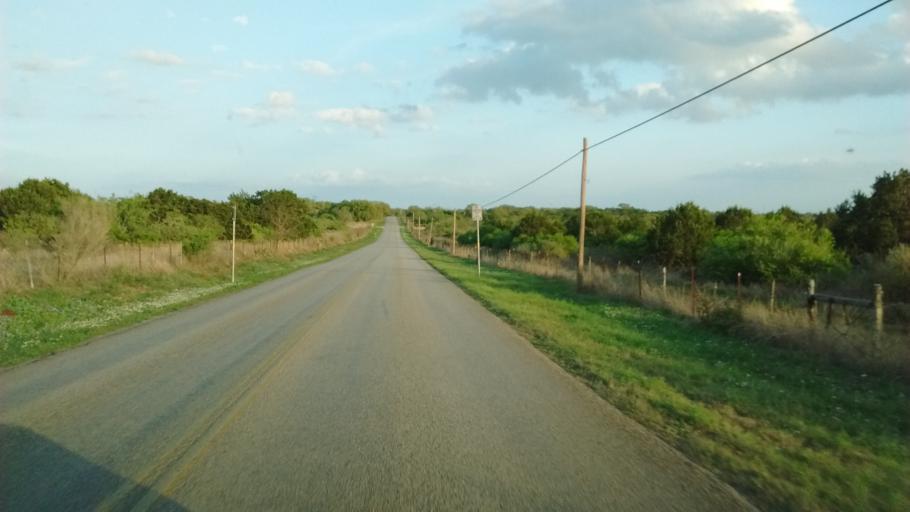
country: US
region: Texas
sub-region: Comal County
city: New Braunfels
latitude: 29.7442
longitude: -98.1394
